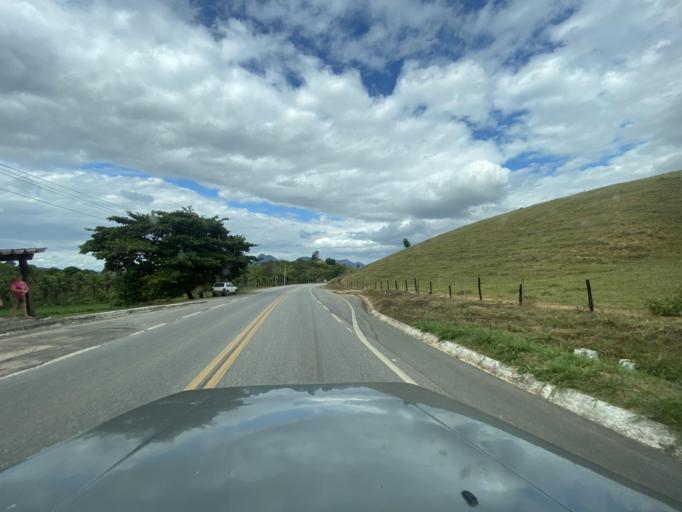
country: BR
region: Espirito Santo
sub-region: Jeronimo Monteiro
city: Jeronimo Monteiro
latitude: -20.7754
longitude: -41.4220
